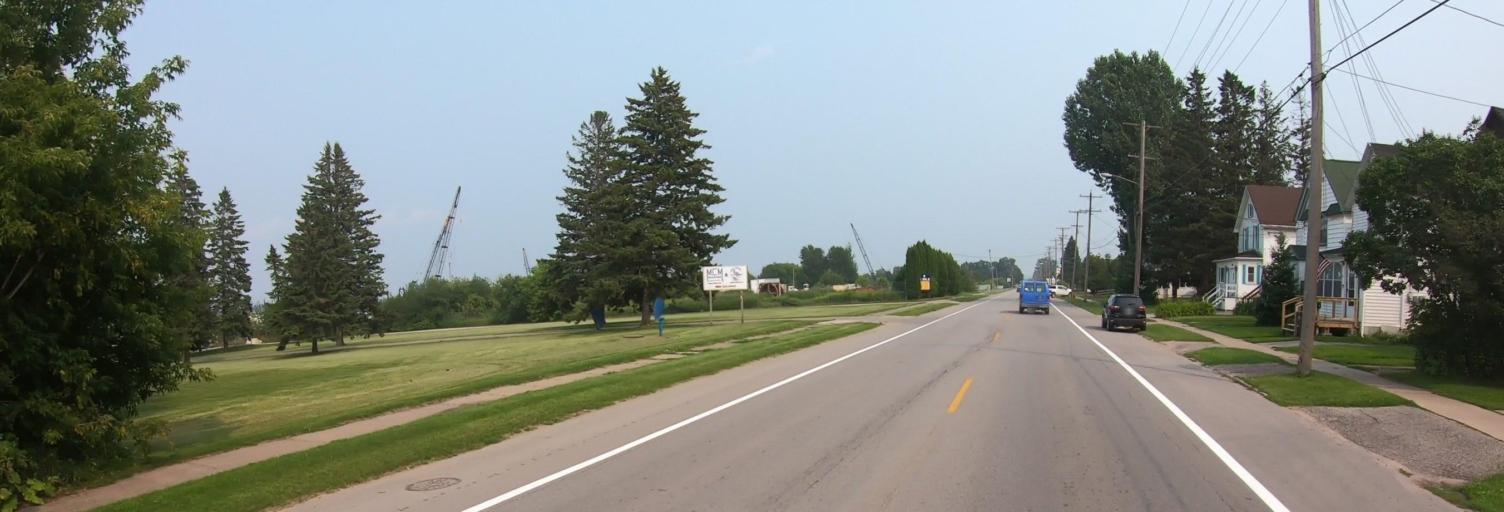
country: US
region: Michigan
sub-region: Chippewa County
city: Sault Ste. Marie
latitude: 46.4921
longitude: -84.3219
